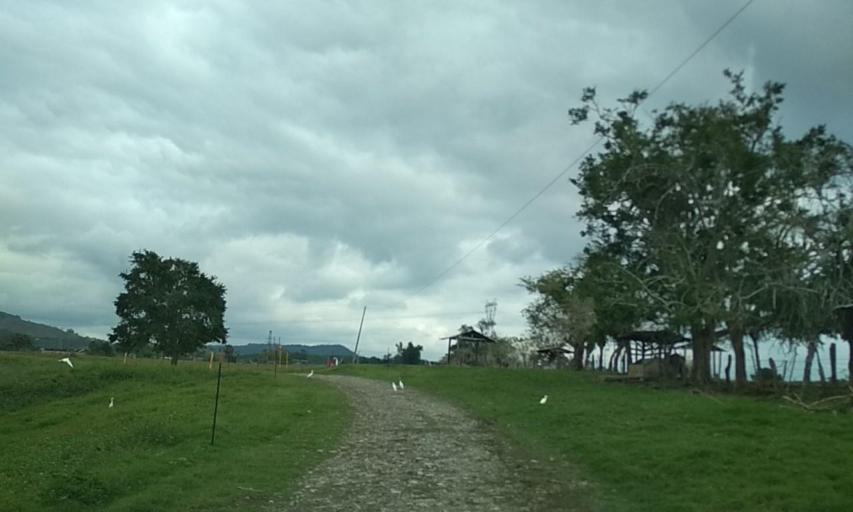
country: MX
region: Veracruz
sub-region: Papantla
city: El Chote
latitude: 20.3913
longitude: -97.3430
